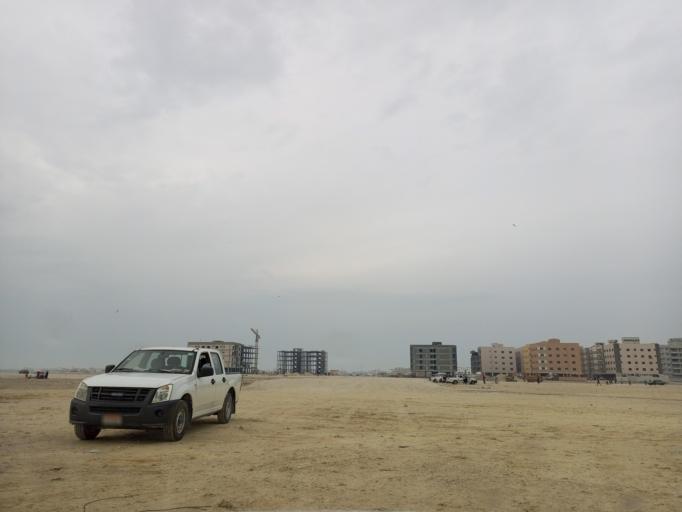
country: BH
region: Muharraq
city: Al Hadd
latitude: 26.2274
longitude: 50.6434
